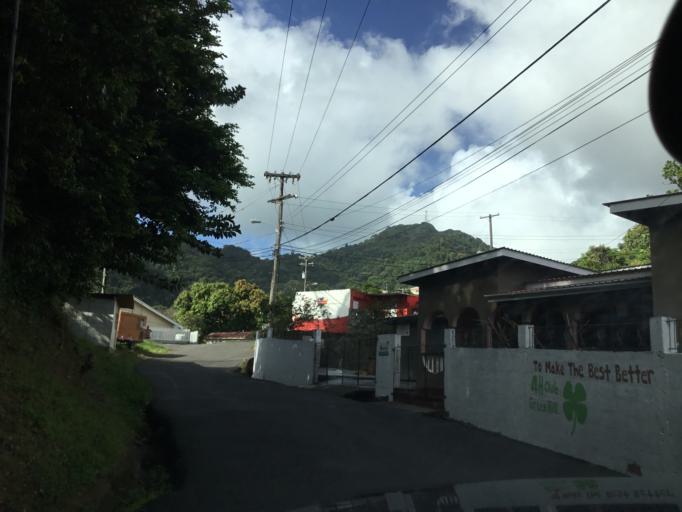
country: VC
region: Saint George
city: Kingstown
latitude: 13.1717
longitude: -61.2189
